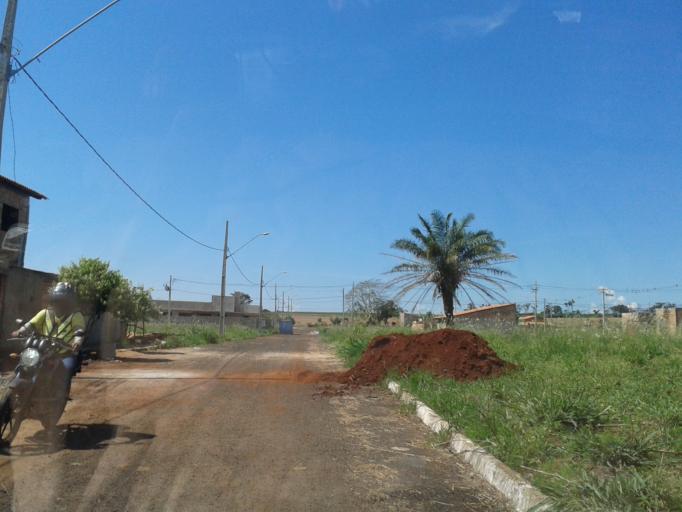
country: BR
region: Goias
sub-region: Itumbiara
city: Itumbiara
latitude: -18.4220
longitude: -49.1832
